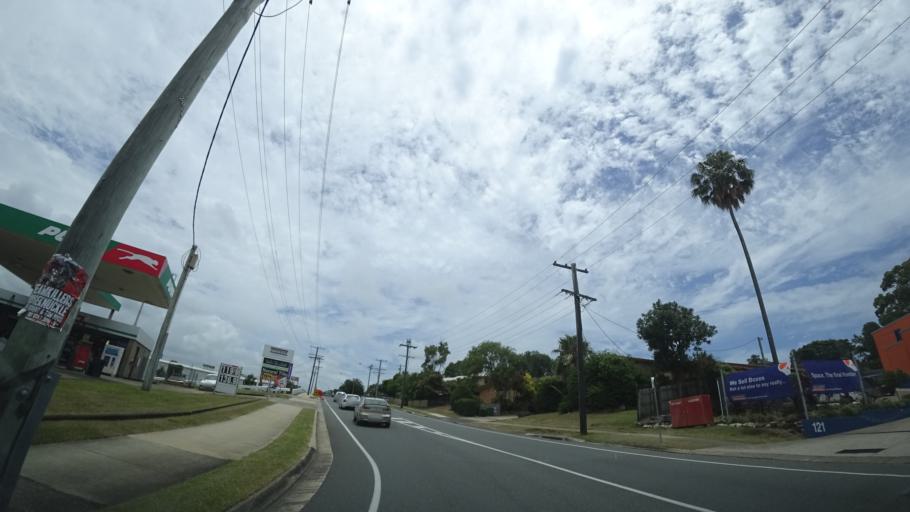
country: AU
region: Queensland
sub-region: Sunshine Coast
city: Mooloolaba
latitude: -26.6709
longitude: 153.0959
